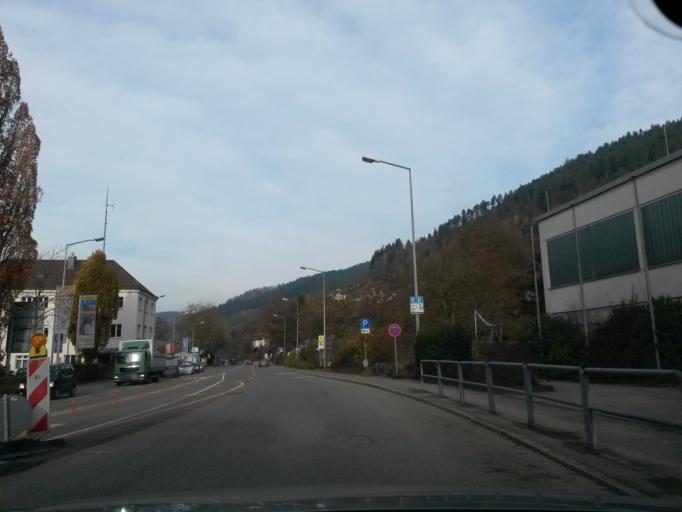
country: DE
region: Baden-Wuerttemberg
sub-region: Freiburg Region
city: Schramberg
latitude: 48.2284
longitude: 8.3846
